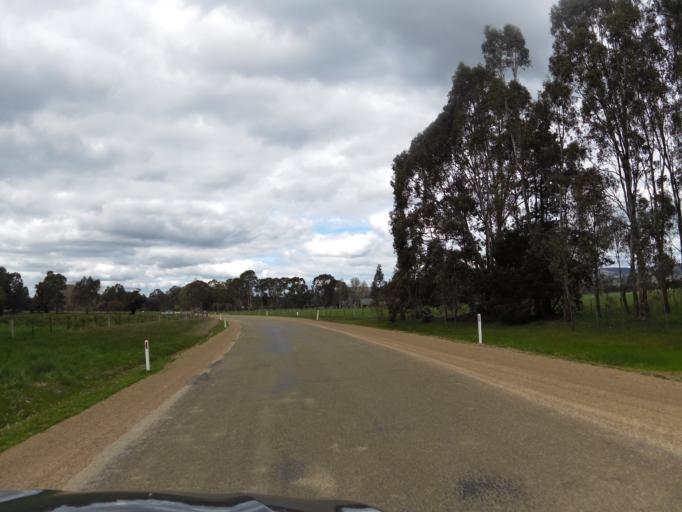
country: AU
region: Victoria
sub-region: Benalla
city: Benalla
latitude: -36.6503
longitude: 145.8847
